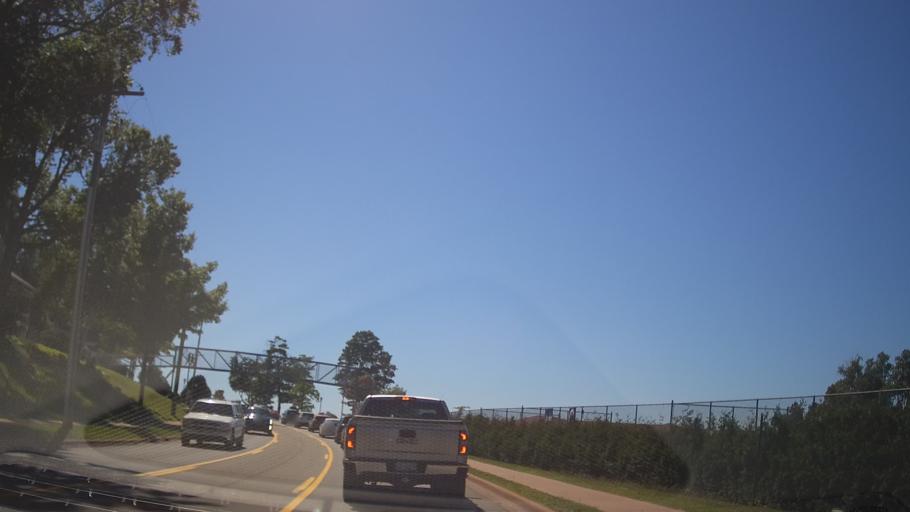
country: US
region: Michigan
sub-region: Emmet County
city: Petoskey
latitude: 45.3860
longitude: -84.9357
